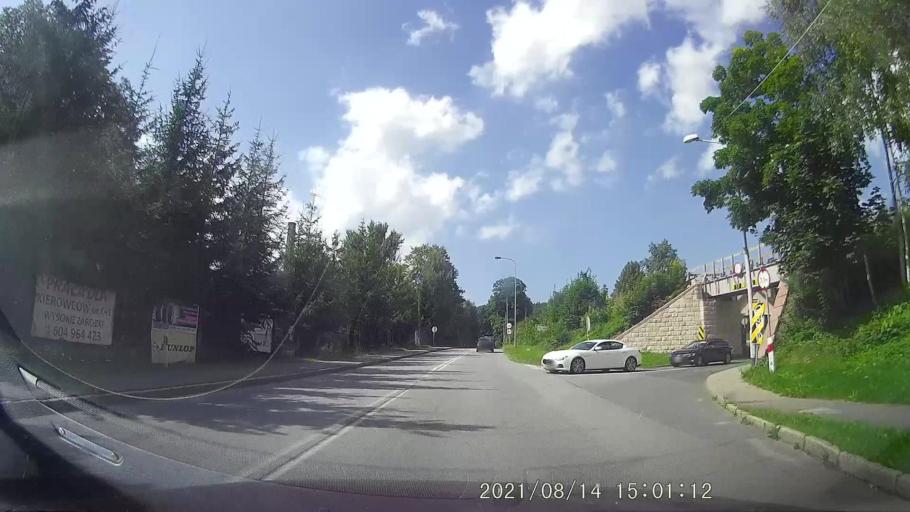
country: PL
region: Lower Silesian Voivodeship
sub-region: Powiat walbrzyski
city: Jedlina-Zdroj
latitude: 50.7177
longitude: 16.3489
